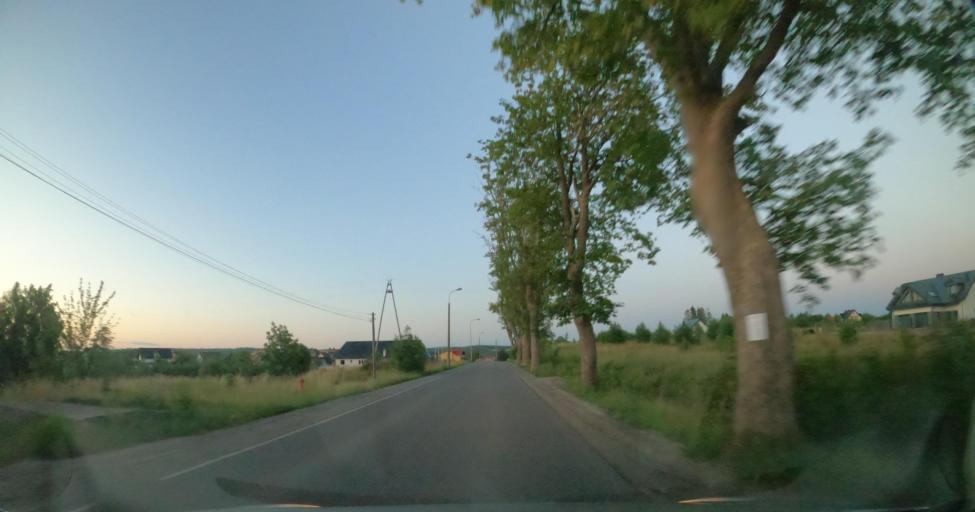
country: PL
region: Pomeranian Voivodeship
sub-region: Powiat wejherowski
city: Szemud
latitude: 54.4838
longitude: 18.2130
